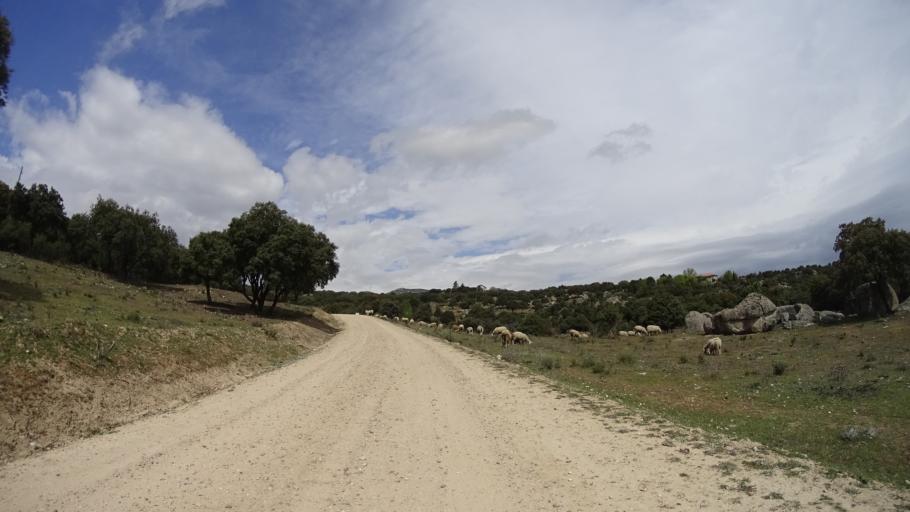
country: ES
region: Madrid
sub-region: Provincia de Madrid
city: Hoyo de Manzanares
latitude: 40.6193
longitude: -3.8823
